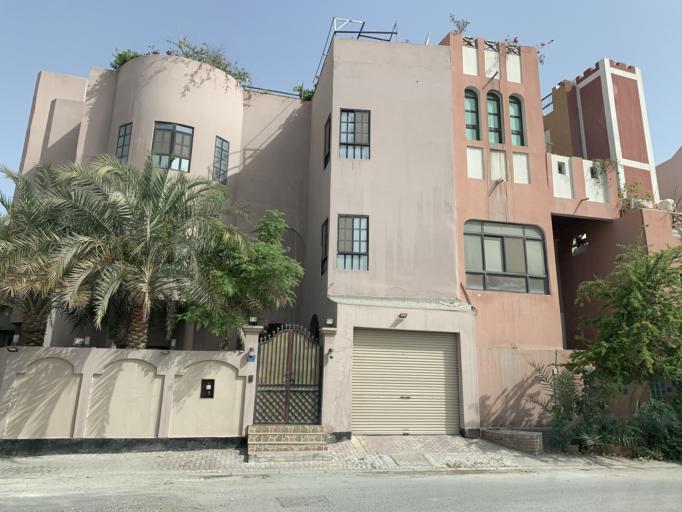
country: BH
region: Northern
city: Sitrah
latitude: 26.1319
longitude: 50.5972
